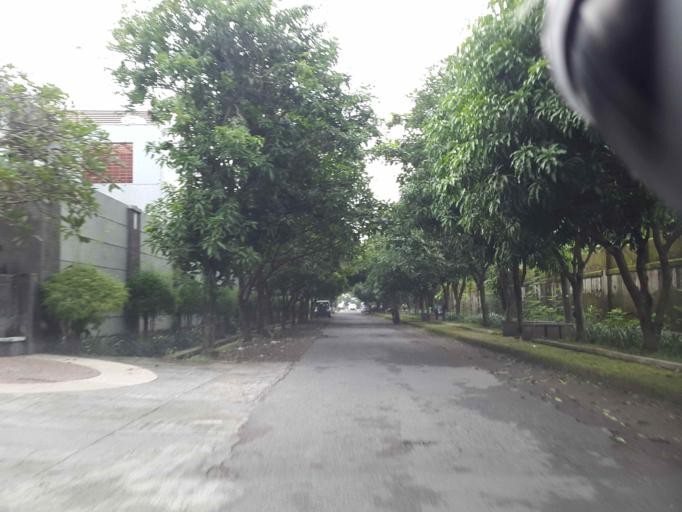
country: ID
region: Central Java
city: Surakarta
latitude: -7.5601
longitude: 110.8011
